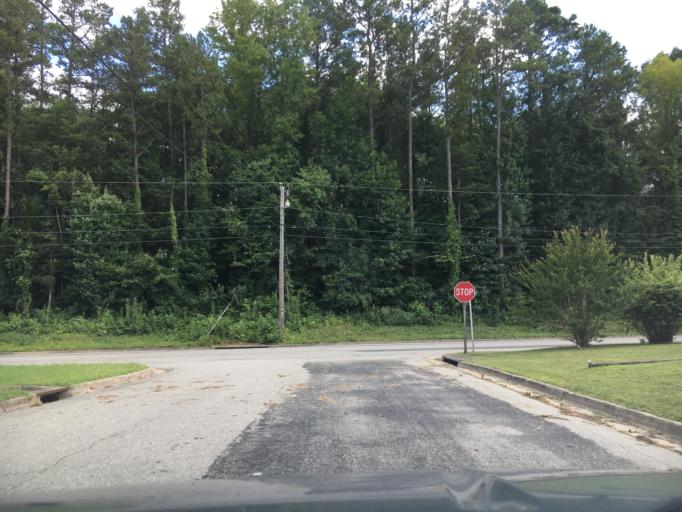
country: US
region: Virginia
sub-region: Halifax County
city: South Boston
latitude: 36.7110
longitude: -78.8949
